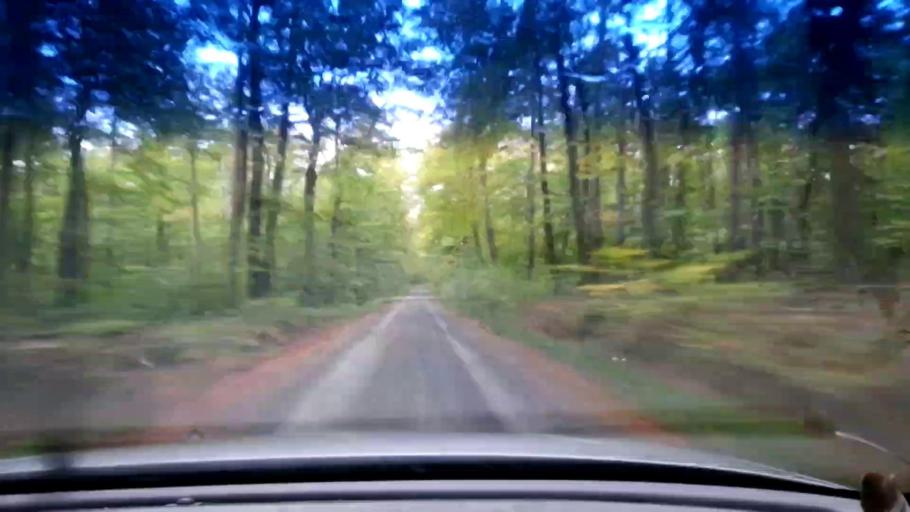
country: DE
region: Bavaria
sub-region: Upper Franconia
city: Burgwindheim
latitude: 49.8512
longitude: 10.6404
